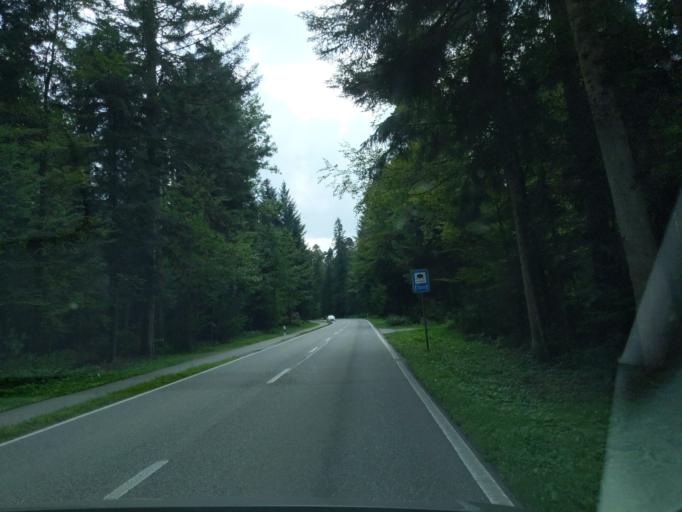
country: CH
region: Bern
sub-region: Oberaargau
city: Wyssachen
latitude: 47.1037
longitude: 7.8272
